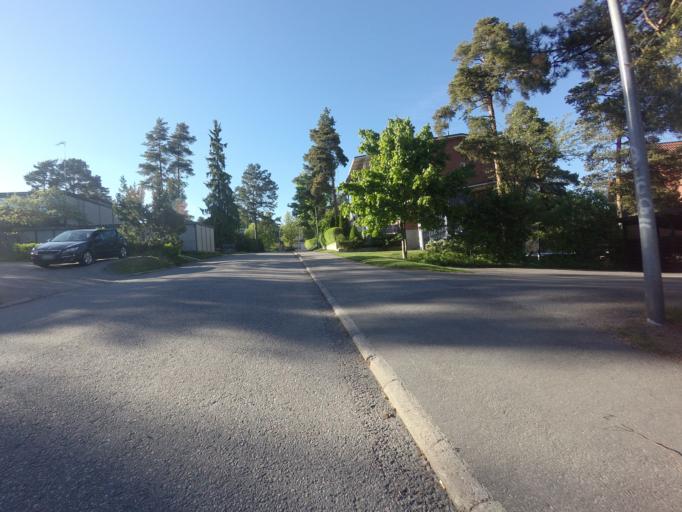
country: FI
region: Uusimaa
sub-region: Helsinki
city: Koukkuniemi
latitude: 60.1736
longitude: 24.7345
